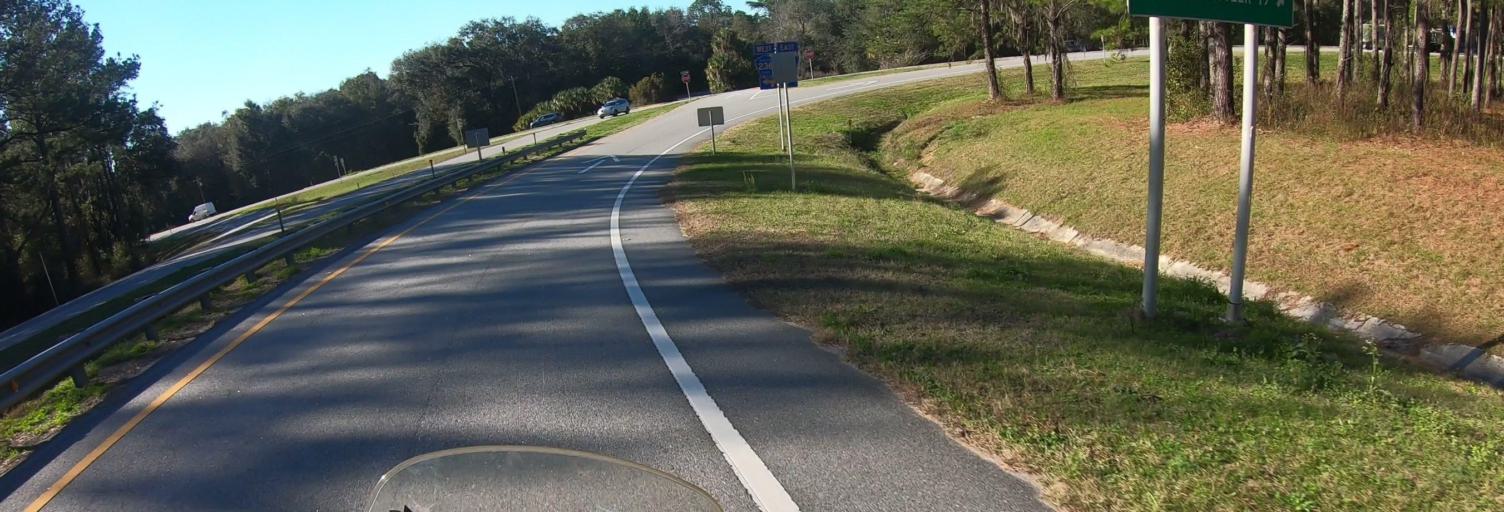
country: US
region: Florida
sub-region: Alachua County
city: High Springs
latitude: 29.8717
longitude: -82.5442
